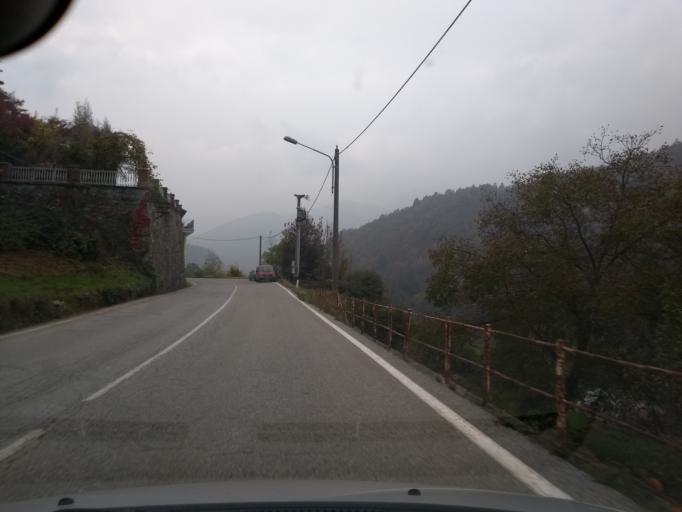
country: IT
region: Piedmont
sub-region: Provincia di Torino
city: Ceres
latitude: 45.3075
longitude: 7.3949
